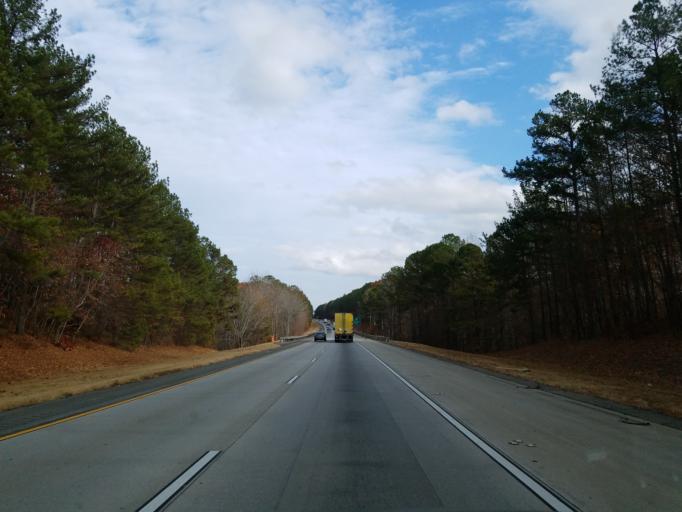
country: US
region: Georgia
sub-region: Haralson County
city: Tallapoosa
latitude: 33.6817
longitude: -85.2793
